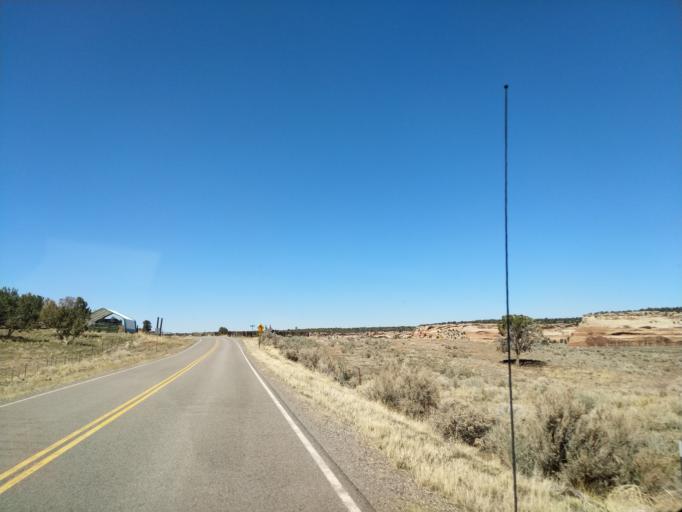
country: US
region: Colorado
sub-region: Mesa County
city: Fruita
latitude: 39.0021
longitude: -108.8372
